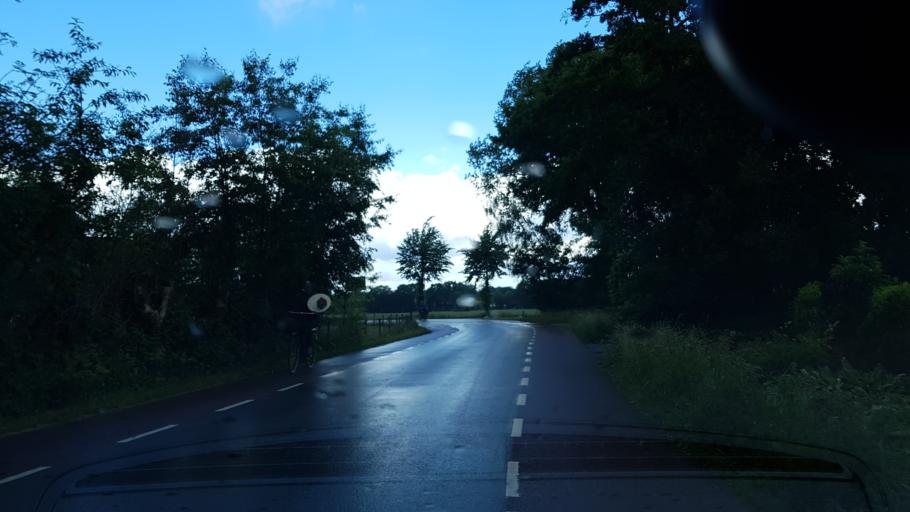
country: NL
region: Gelderland
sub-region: Gemeente Ermelo
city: Horst
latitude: 52.2982
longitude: 5.5848
